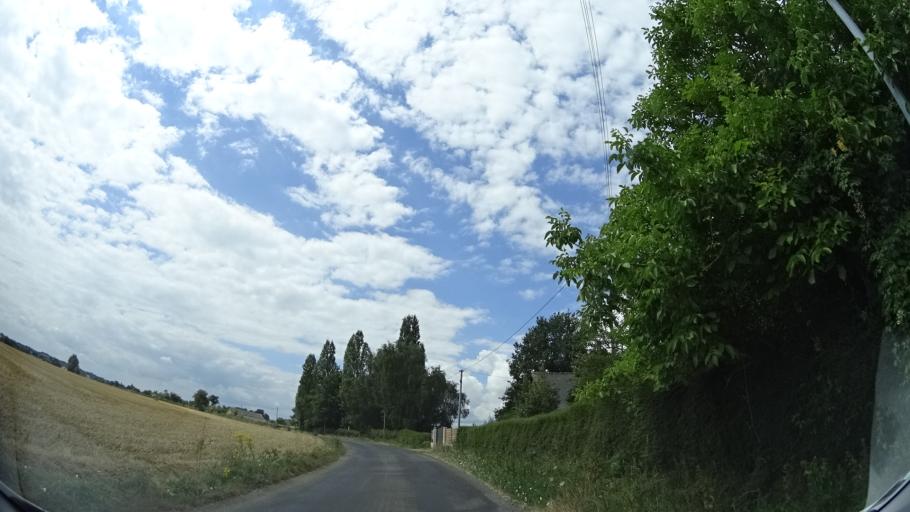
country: FR
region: Brittany
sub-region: Departement d'Ille-et-Vilaine
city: Pace
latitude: 48.1702
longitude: -1.7578
